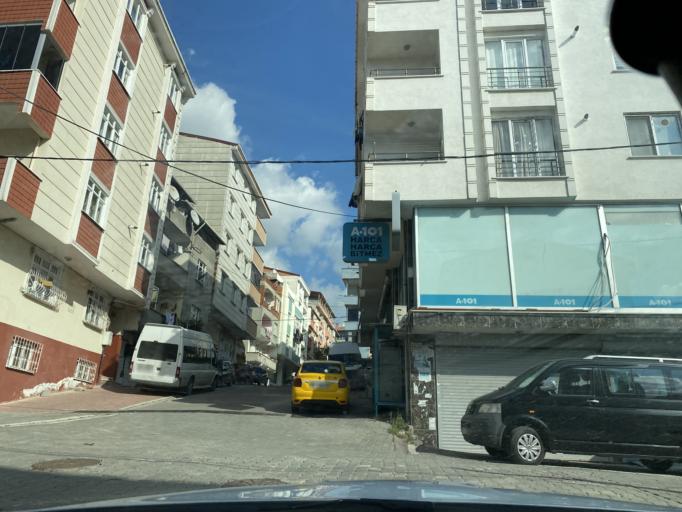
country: TR
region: Istanbul
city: Esenyurt
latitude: 41.0303
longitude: 28.6666
